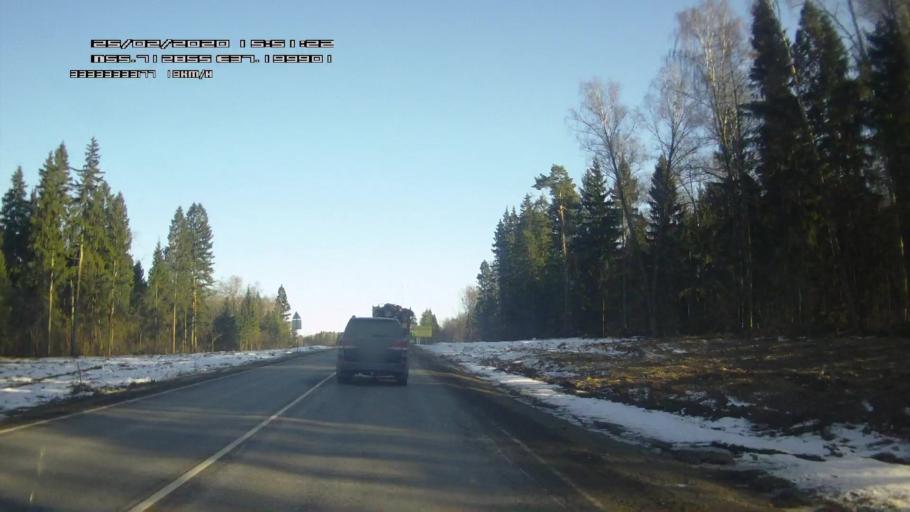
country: RU
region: Moskovskaya
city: Gorki Vtoryye
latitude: 55.7129
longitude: 37.1995
